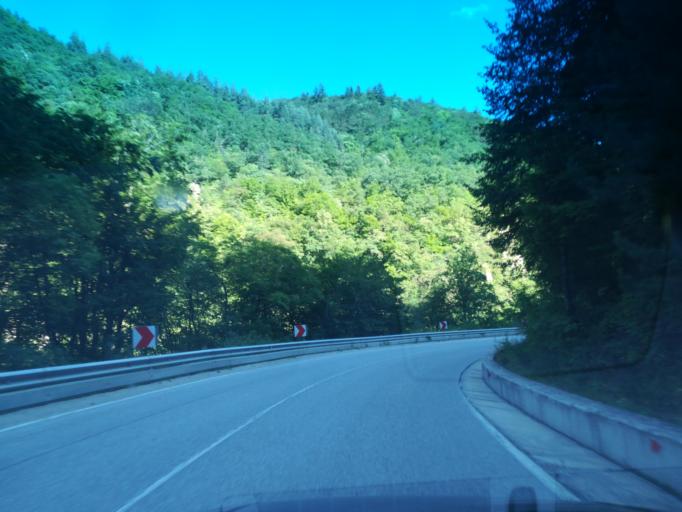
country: BG
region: Smolyan
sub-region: Obshtina Chepelare
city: Chepelare
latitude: 41.7792
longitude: 24.7078
